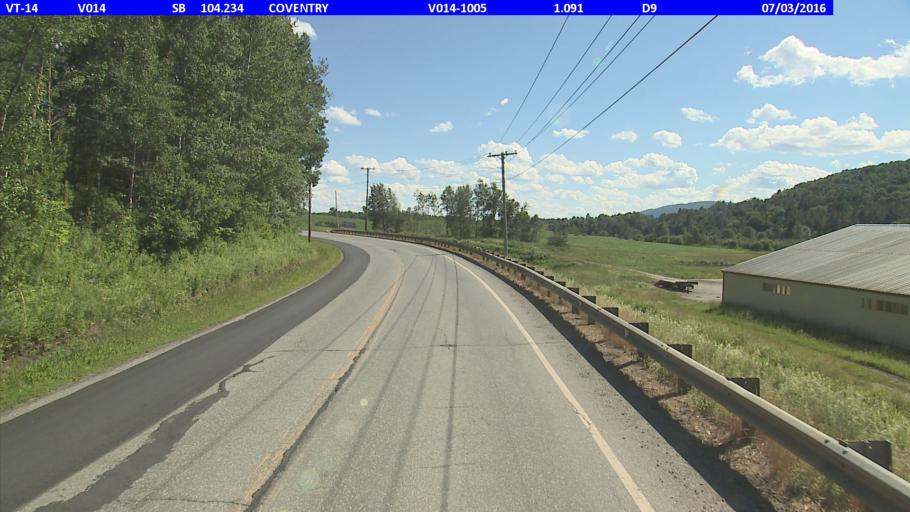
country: US
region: Vermont
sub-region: Orleans County
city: Newport
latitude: 44.8798
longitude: -72.2652
